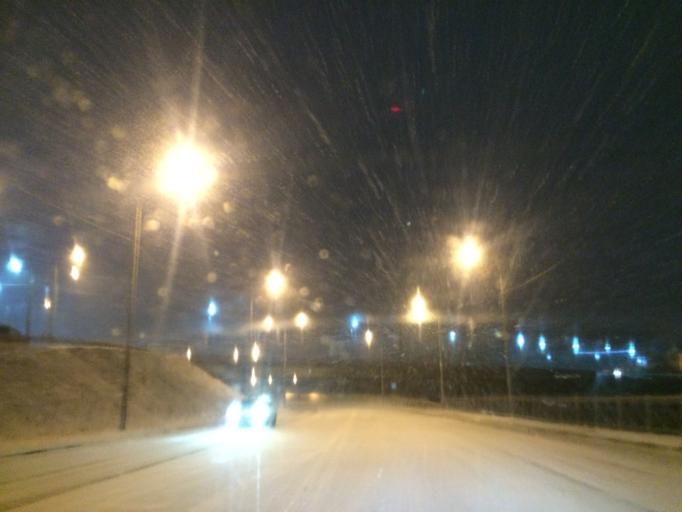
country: RU
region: Tula
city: Tula
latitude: 54.1953
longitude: 37.6303
